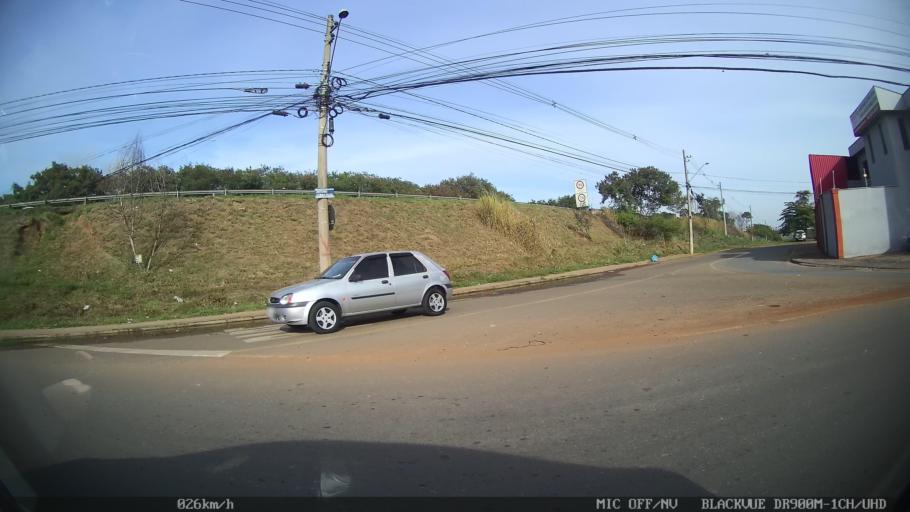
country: BR
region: Sao Paulo
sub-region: Piracicaba
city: Piracicaba
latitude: -22.6852
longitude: -47.6734
